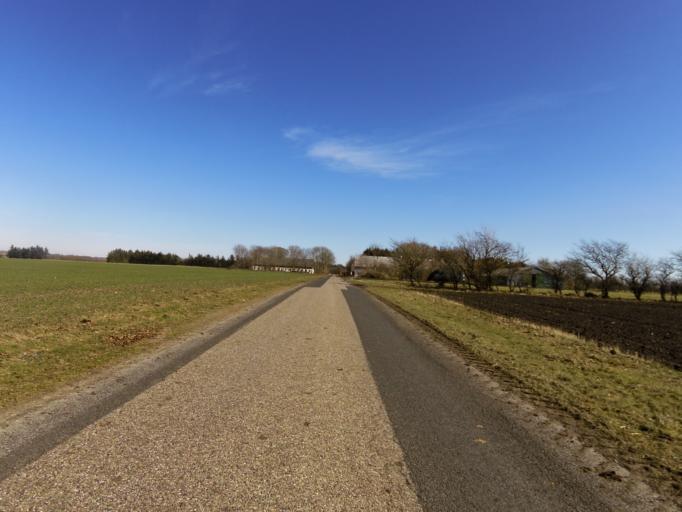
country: DK
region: South Denmark
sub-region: Tonder Kommune
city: Toftlund
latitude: 55.2369
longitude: 9.0999
